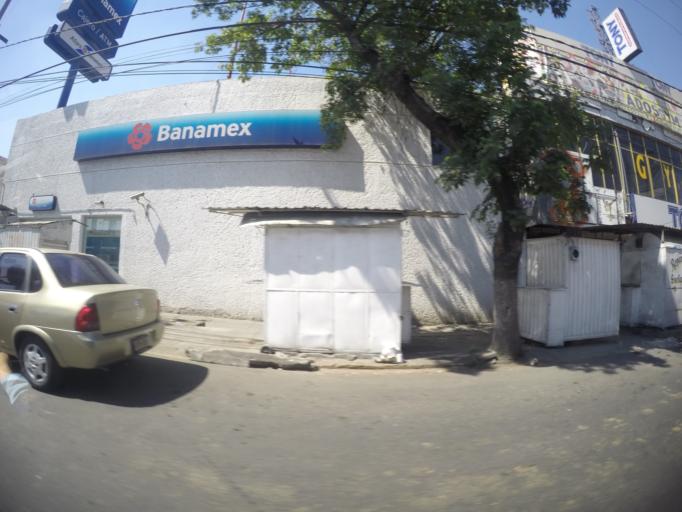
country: MX
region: Mexico
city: Ecatepec
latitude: 19.5958
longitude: -99.0375
